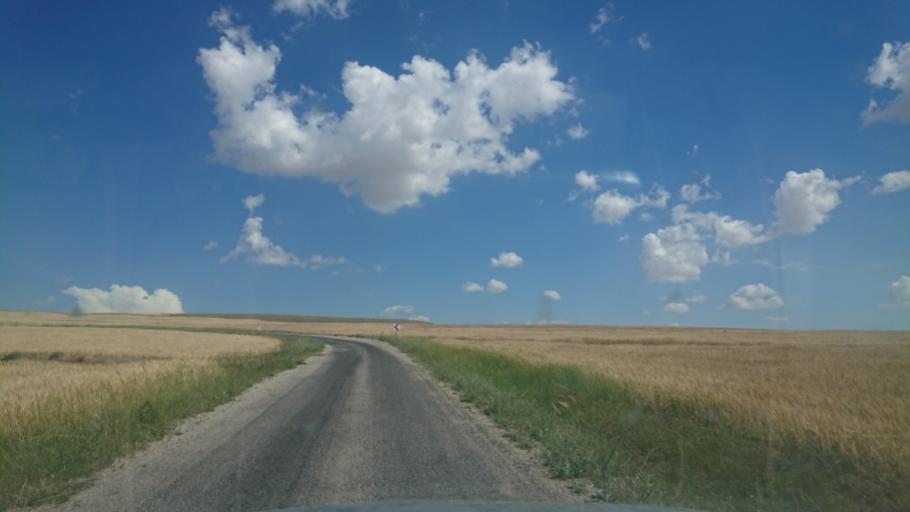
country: TR
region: Aksaray
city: Agacoren
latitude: 38.8068
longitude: 33.8013
